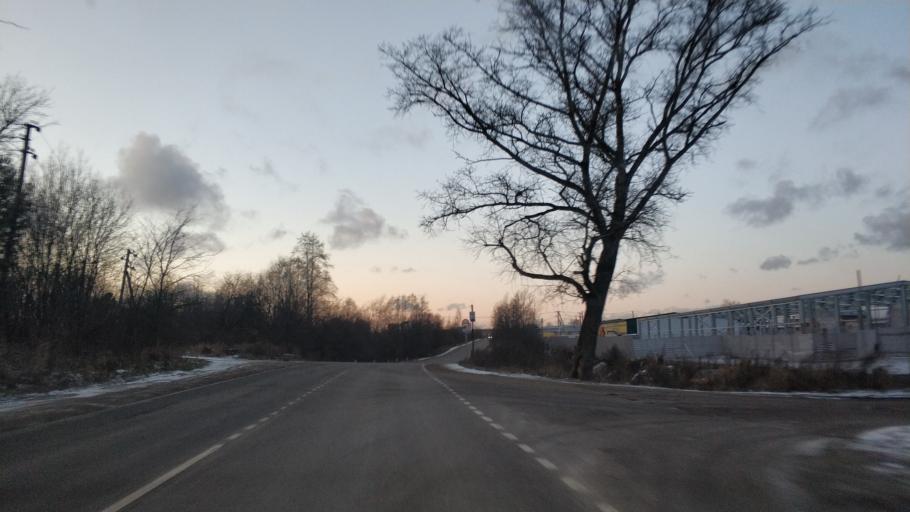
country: RU
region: St.-Petersburg
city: Pontonnyy
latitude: 59.8086
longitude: 30.6151
